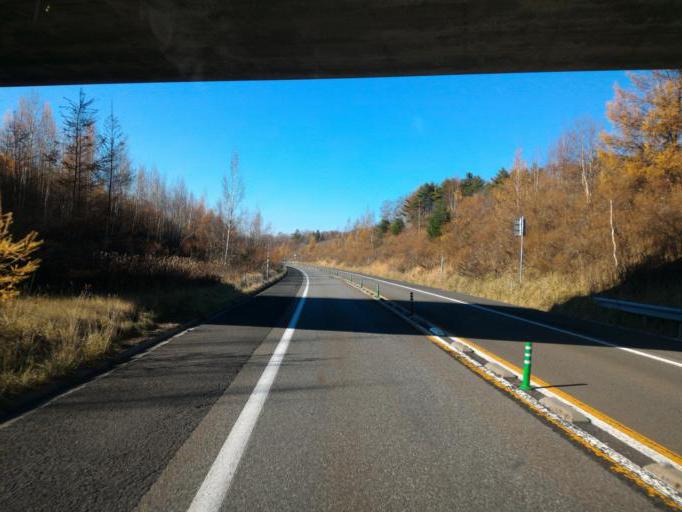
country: JP
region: Hokkaido
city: Chitose
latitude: 42.8981
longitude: 141.8540
